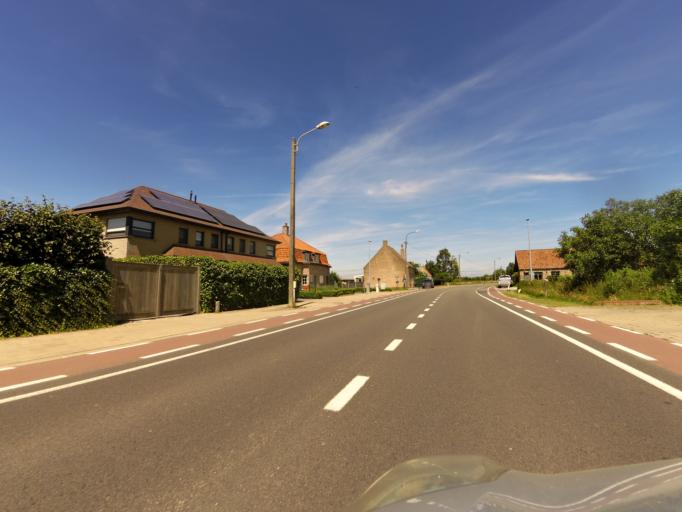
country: BE
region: Flanders
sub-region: Provincie West-Vlaanderen
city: Damme
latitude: 51.2817
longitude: 3.2342
